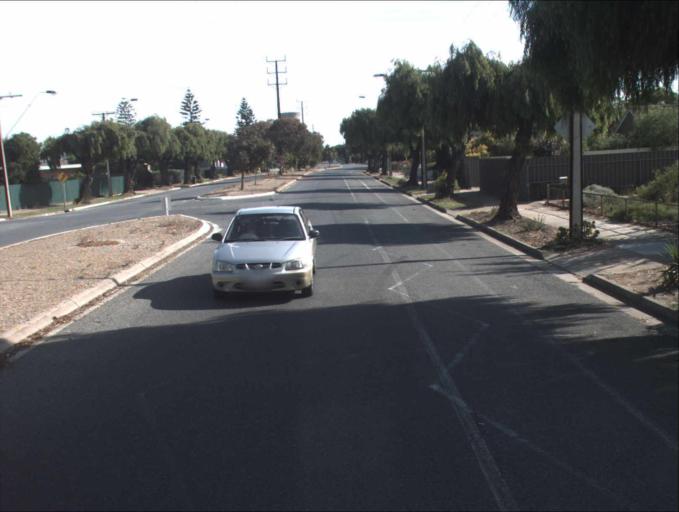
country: AU
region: South Australia
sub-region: Port Adelaide Enfield
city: Birkenhead
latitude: -34.8032
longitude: 138.4966
